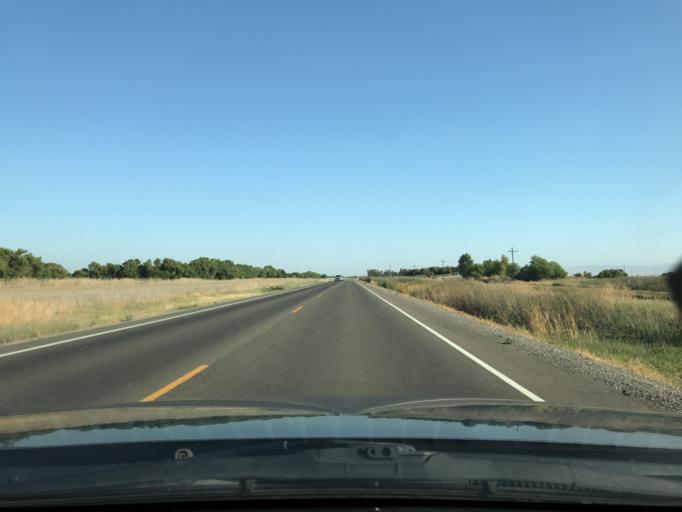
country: US
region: California
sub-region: Merced County
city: Los Banos
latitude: 37.1710
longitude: -120.8320
